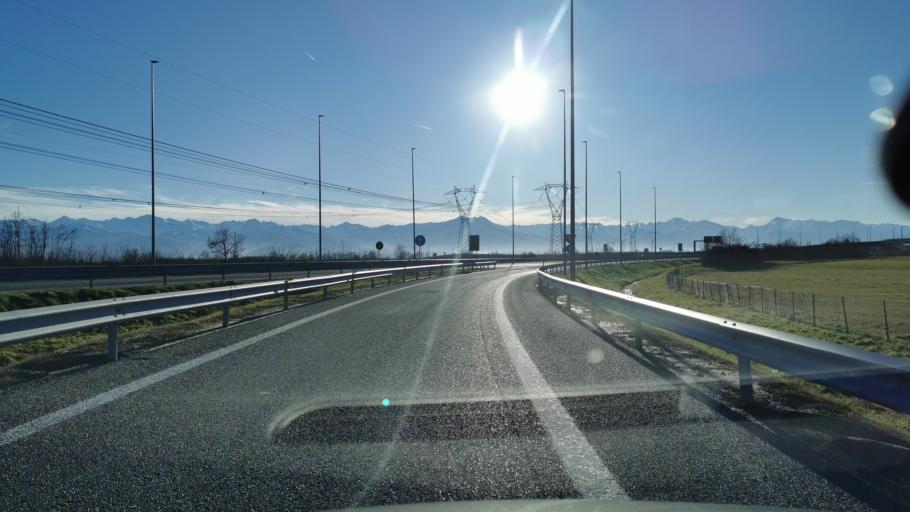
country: IT
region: Piedmont
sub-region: Provincia di Cuneo
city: Magliano Alpi
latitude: 44.4868
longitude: 7.8155
